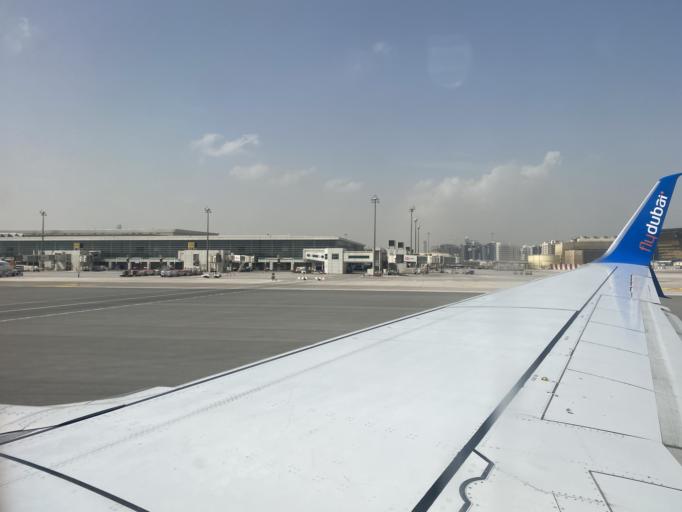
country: AE
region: Ash Shariqah
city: Sharjah
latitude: 25.2622
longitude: 55.3424
